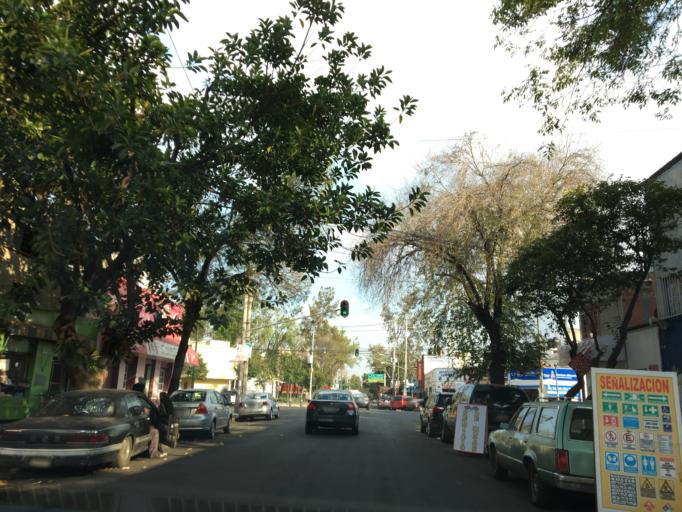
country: MX
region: Mexico City
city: Mexico City
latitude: 19.4179
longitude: -99.1452
